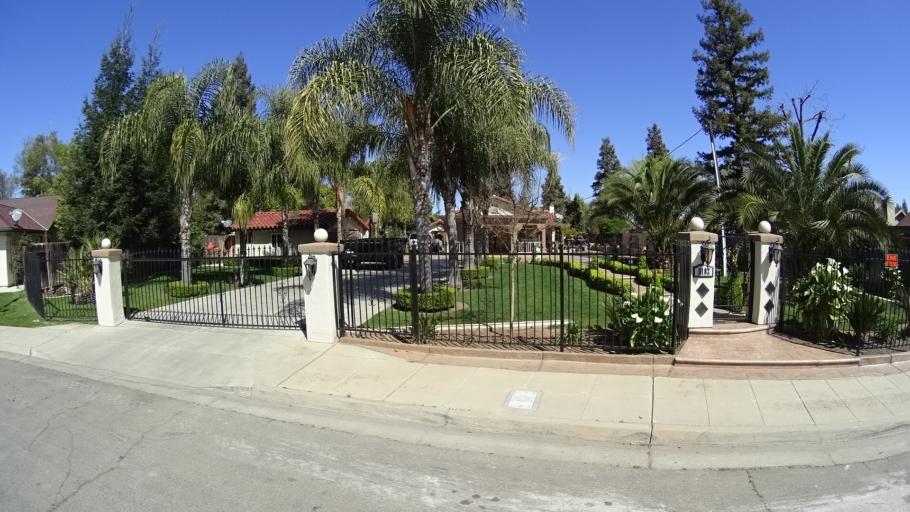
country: US
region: California
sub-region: Fresno County
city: West Park
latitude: 36.7856
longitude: -119.8837
